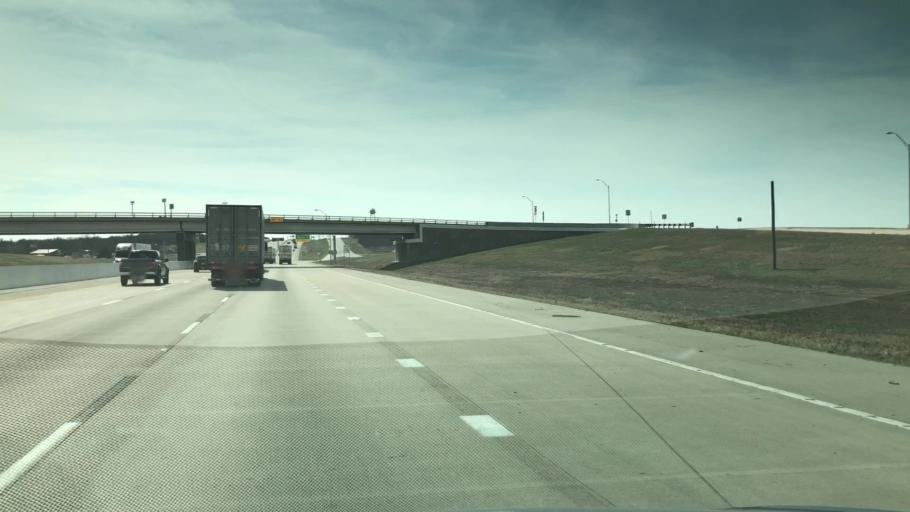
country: US
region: Texas
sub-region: McLennan County
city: West
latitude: 31.8392
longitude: -97.0896
